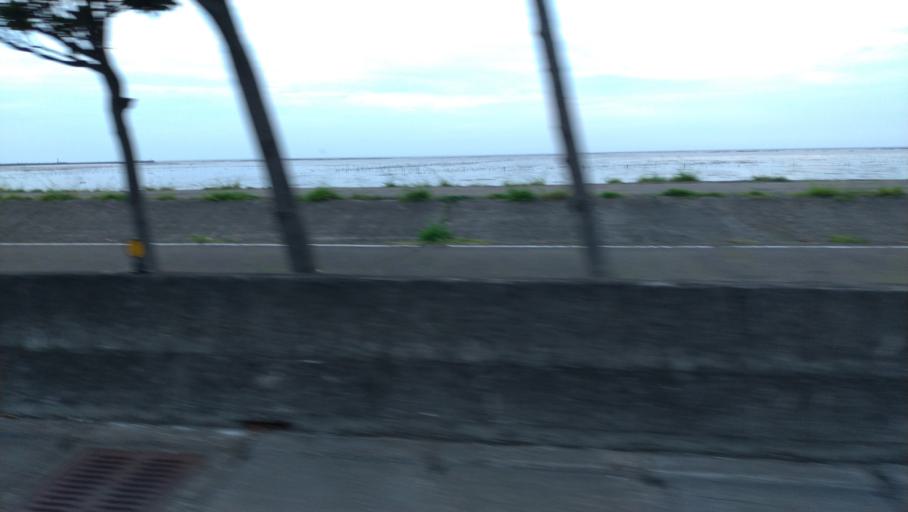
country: TW
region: Taiwan
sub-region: Hsinchu
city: Hsinchu
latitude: 24.7743
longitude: 120.9140
